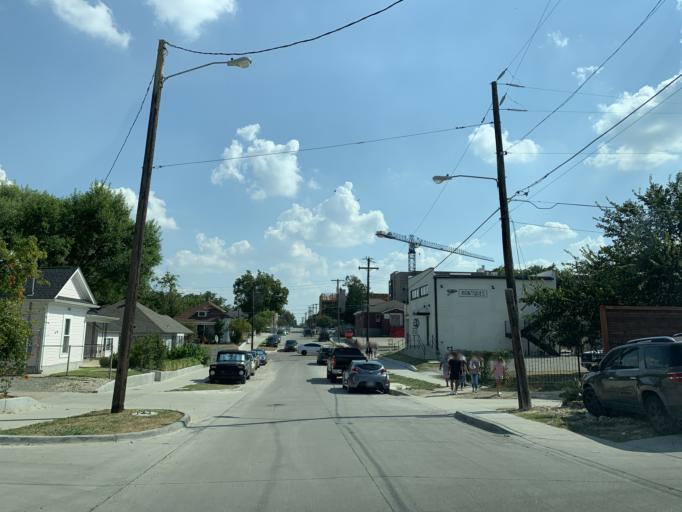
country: US
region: Texas
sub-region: Dallas County
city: Dallas
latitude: 32.7487
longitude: -96.8265
